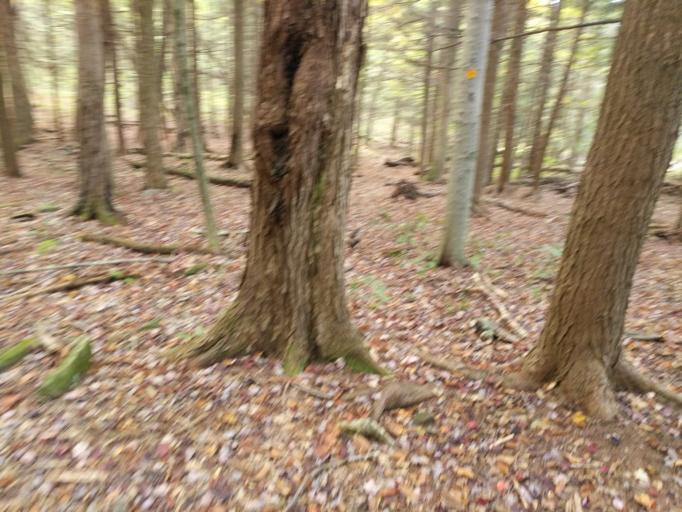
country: US
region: New York
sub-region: Sullivan County
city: Livingston Manor
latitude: 41.8724
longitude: -75.0297
